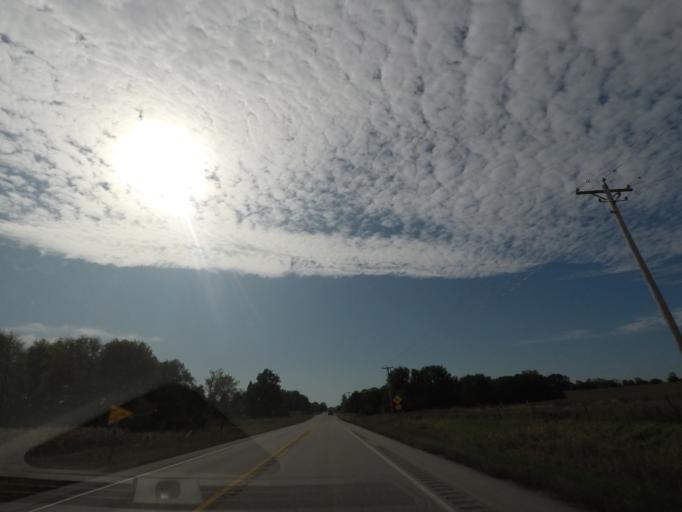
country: US
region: Iowa
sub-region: Story County
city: Gilbert
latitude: 42.0843
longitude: -93.6205
